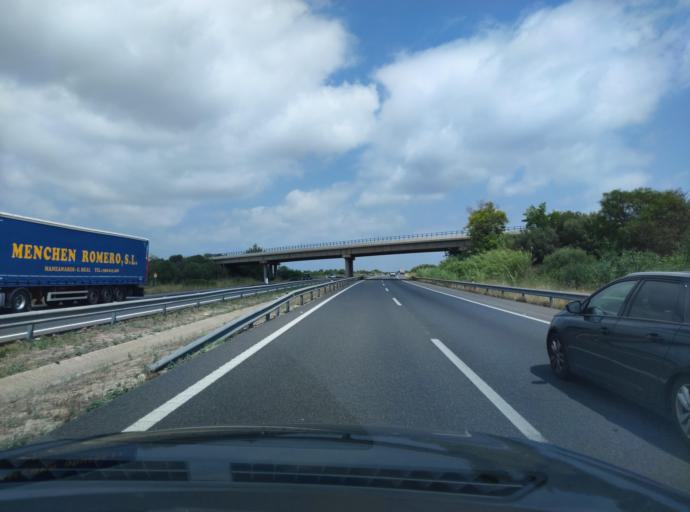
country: ES
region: Valencia
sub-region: Provincia de Castello
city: Vinaros
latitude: 40.4899
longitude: 0.4150
